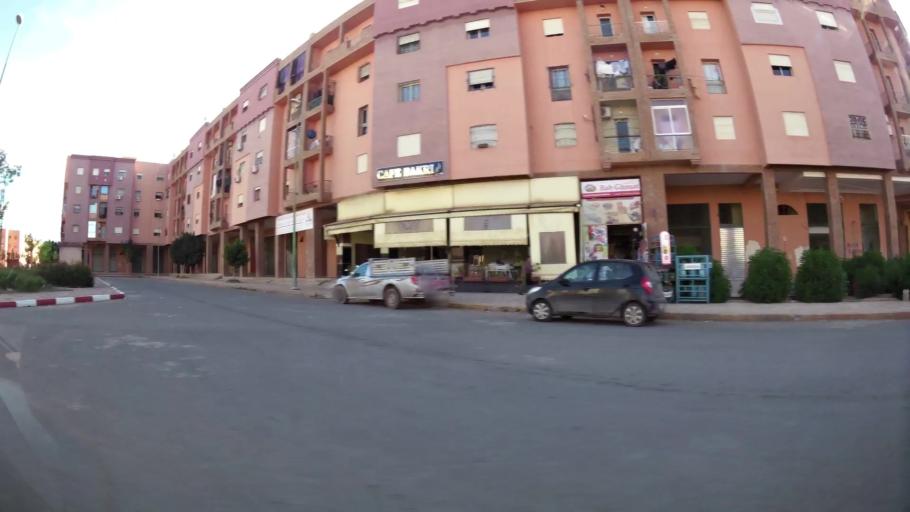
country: MA
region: Marrakech-Tensift-Al Haouz
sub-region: Marrakech
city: Marrakesh
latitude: 31.6864
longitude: -8.0692
